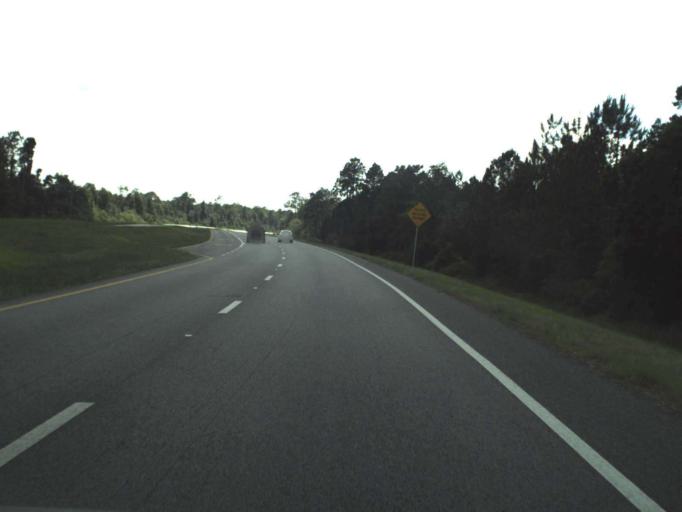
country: US
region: Florida
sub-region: Volusia County
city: Lake Helen
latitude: 29.0295
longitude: -81.1812
